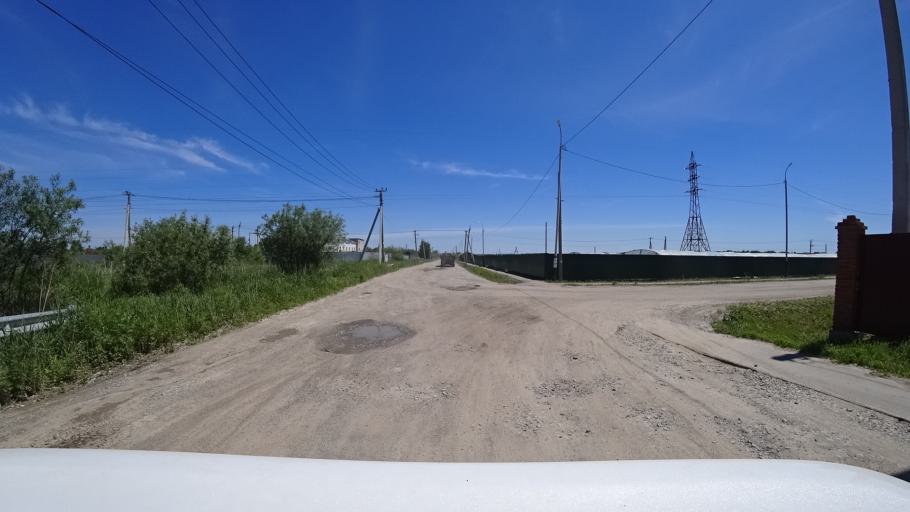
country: RU
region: Khabarovsk Krai
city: Topolevo
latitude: 48.5021
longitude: 135.1838
